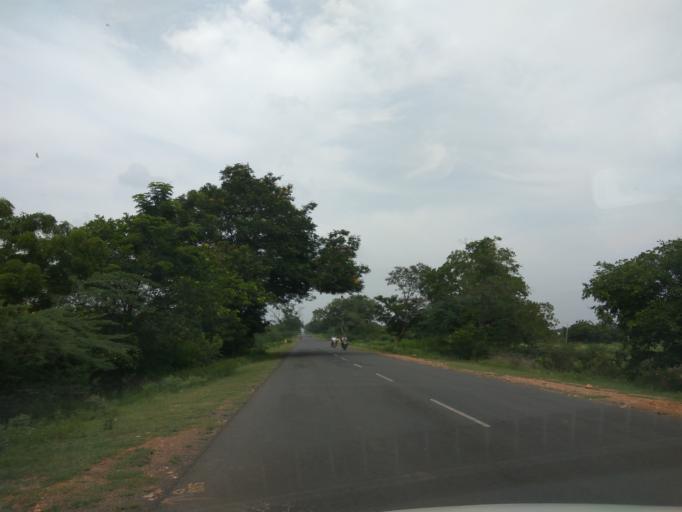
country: IN
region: Andhra Pradesh
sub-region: Prakasam
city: Cumbum
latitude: 15.4976
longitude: 79.0836
